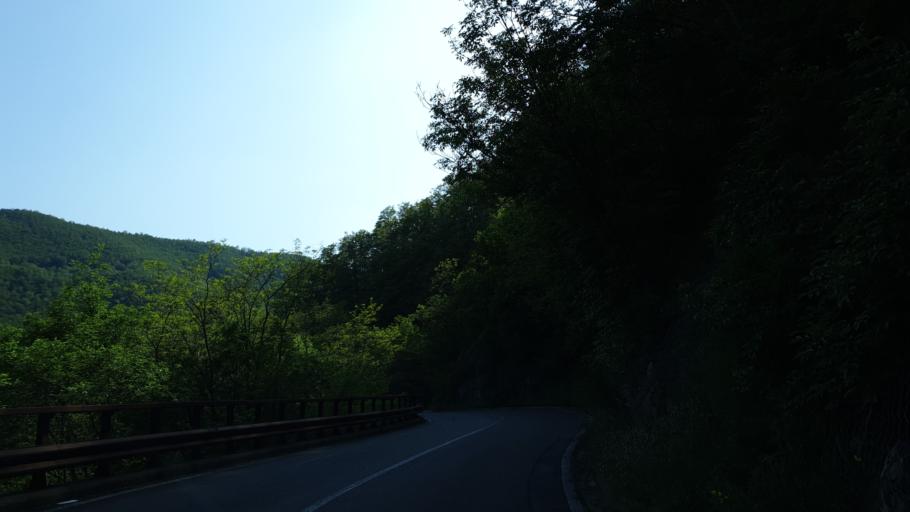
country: IT
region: Tuscany
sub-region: Province of Arezzo
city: Soci
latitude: 43.7731
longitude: 11.8672
